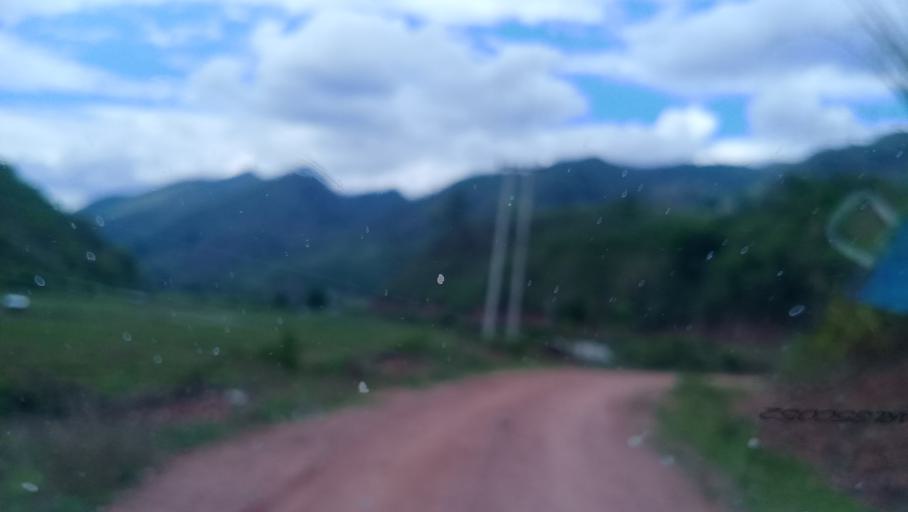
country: CN
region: Yunnan
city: Menglie
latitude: 22.1724
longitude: 101.7441
